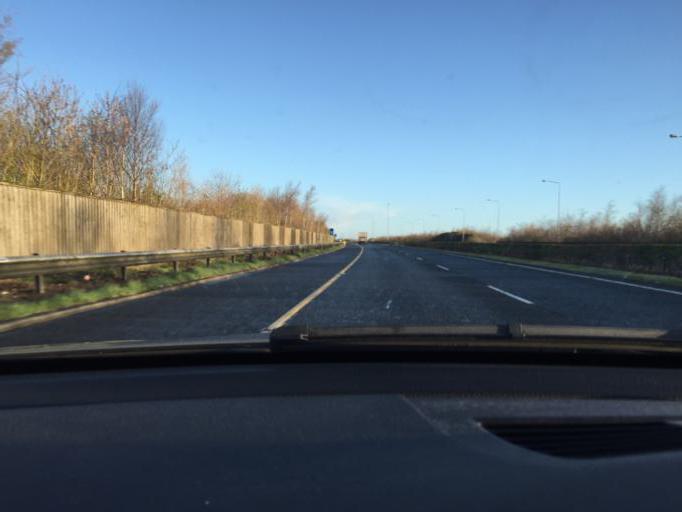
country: IE
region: Leinster
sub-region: Lu
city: Dromiskin
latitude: 53.9606
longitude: -6.4201
